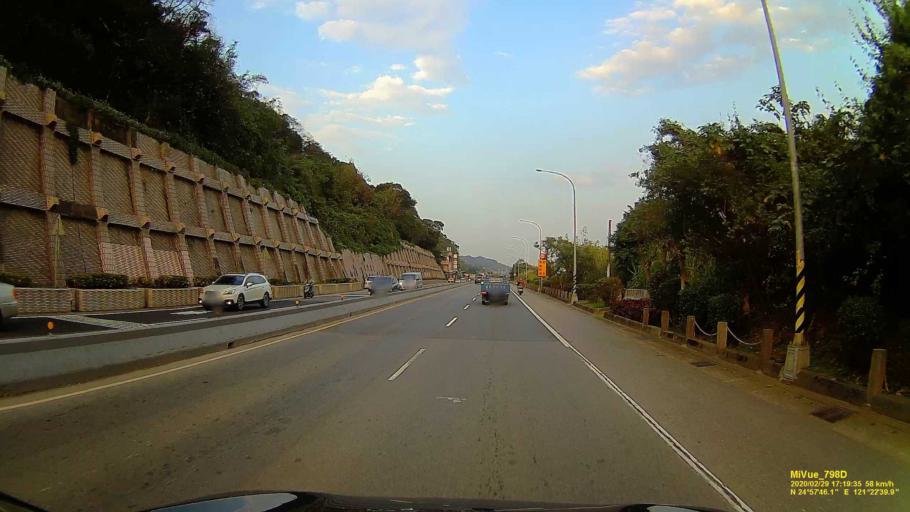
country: TW
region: Taiwan
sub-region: Taoyuan
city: Taoyuan
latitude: 24.9630
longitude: 121.3780
